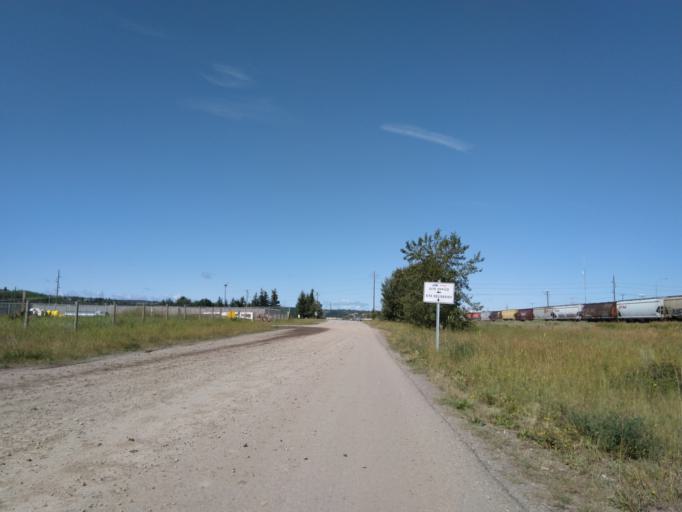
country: CA
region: Alberta
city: Calgary
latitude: 51.1022
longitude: -114.2313
